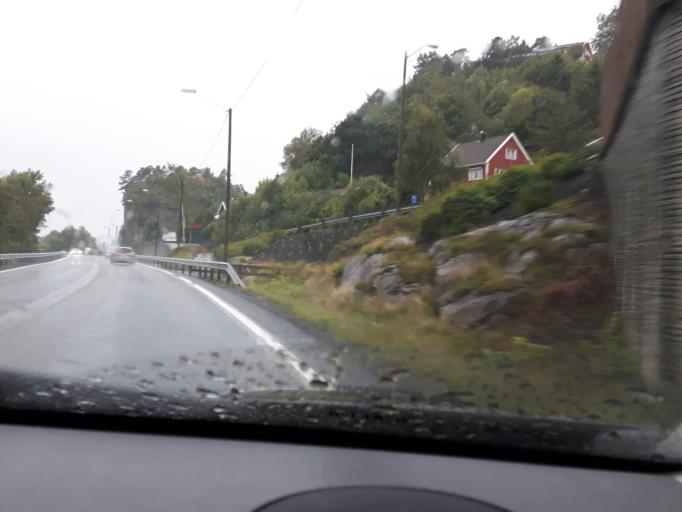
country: NO
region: Vest-Agder
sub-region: Mandal
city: Mandal
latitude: 58.0373
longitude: 7.4422
